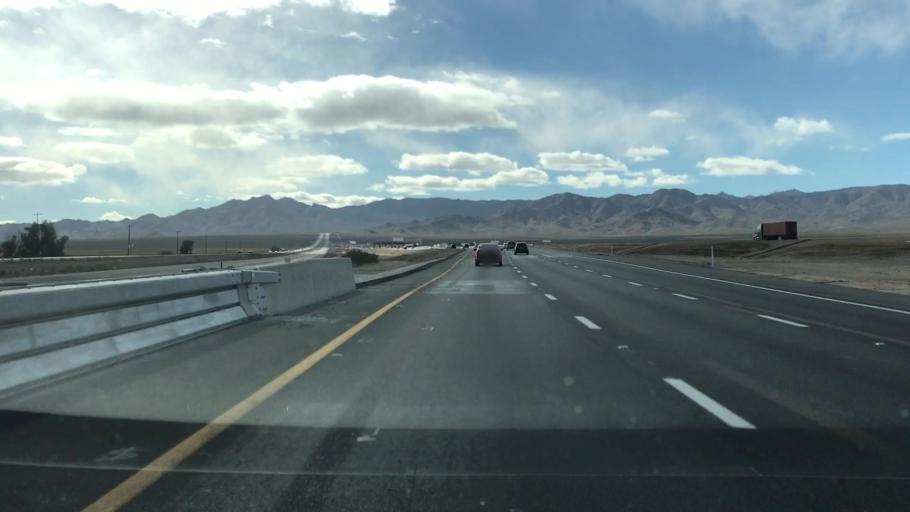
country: US
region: Nevada
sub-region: Clark County
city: Sandy Valley
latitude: 35.5237
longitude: -115.4274
